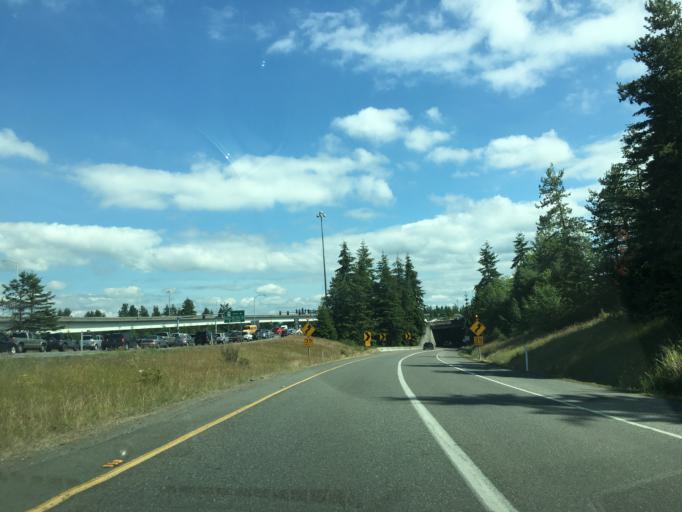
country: US
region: Washington
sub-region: Snohomish County
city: Everett
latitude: 47.9205
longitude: -122.2103
